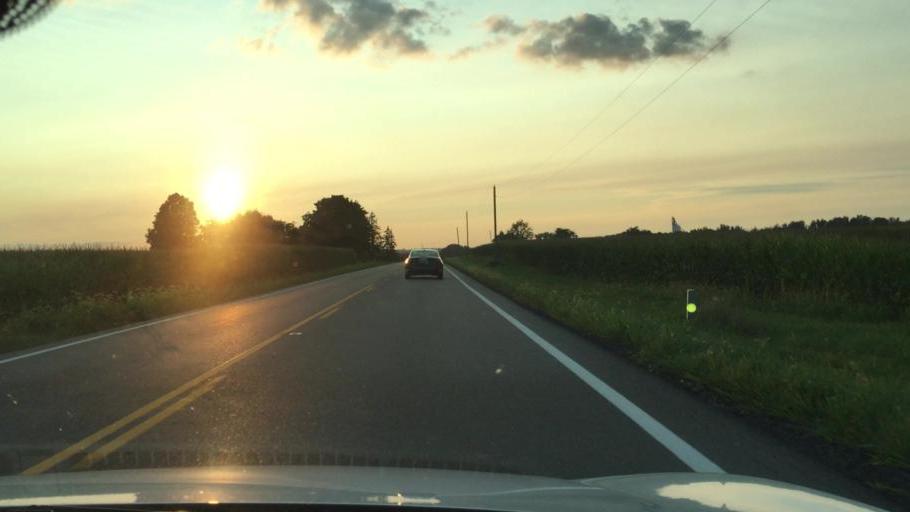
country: US
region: Ohio
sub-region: Champaign County
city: Mechanicsburg
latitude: 40.0609
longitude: -83.5393
